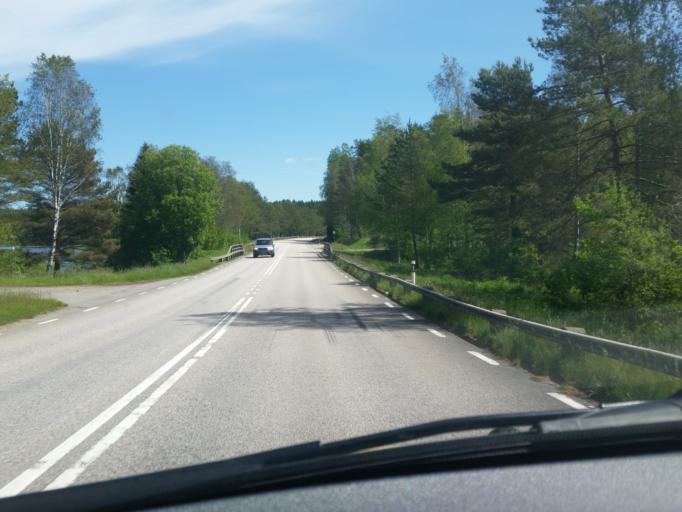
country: SE
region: Vaestra Goetaland
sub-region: Fargelanda Kommun
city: Faergelanda
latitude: 58.5701
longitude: 12.0255
